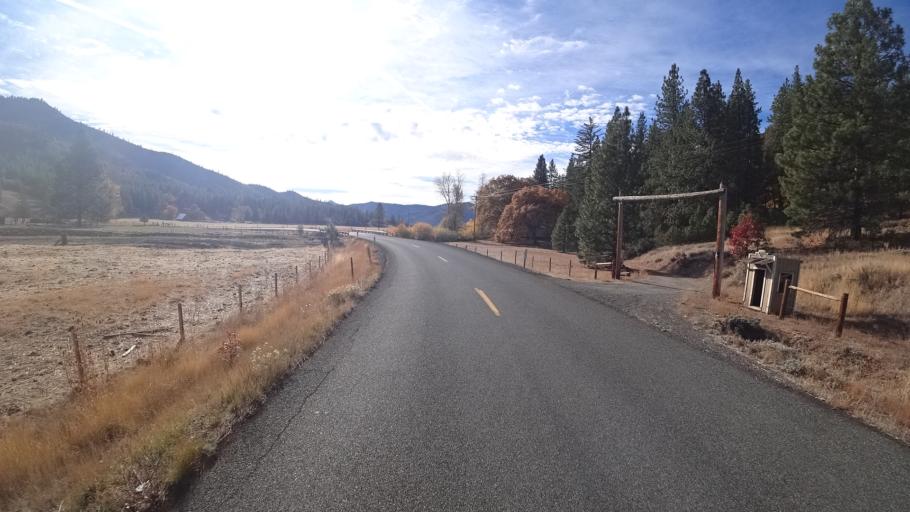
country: US
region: California
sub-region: Siskiyou County
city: Yreka
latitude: 41.6572
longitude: -122.8362
